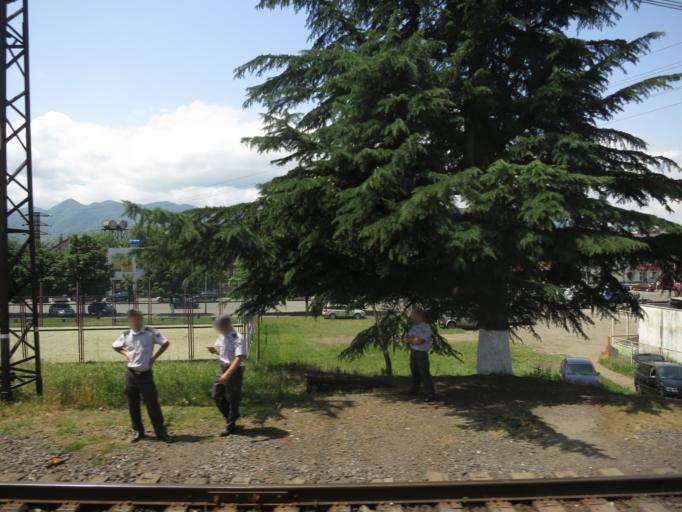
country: GE
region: Imereti
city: Zestap'oni
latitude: 42.1099
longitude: 43.0250
